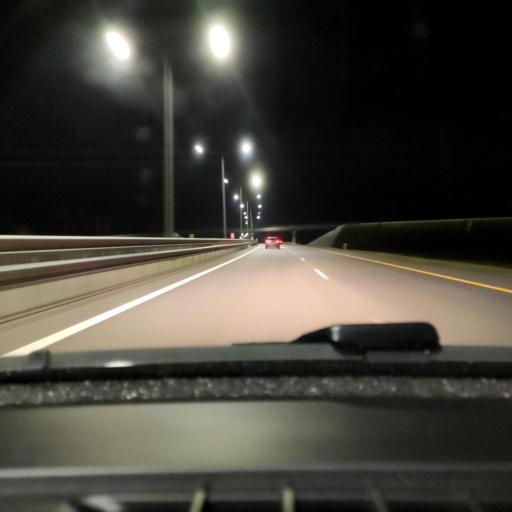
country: RU
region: Voronezj
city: Podkletnoye
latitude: 51.5080
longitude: 39.5148
